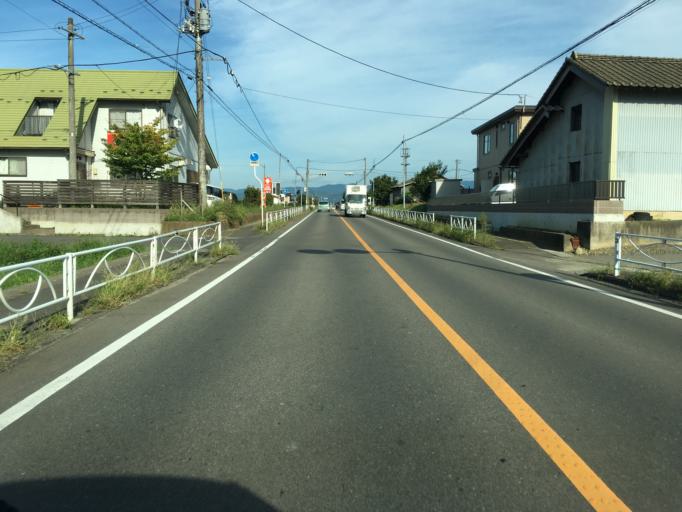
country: JP
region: Fukushima
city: Hobaramachi
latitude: 37.8201
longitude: 140.5221
